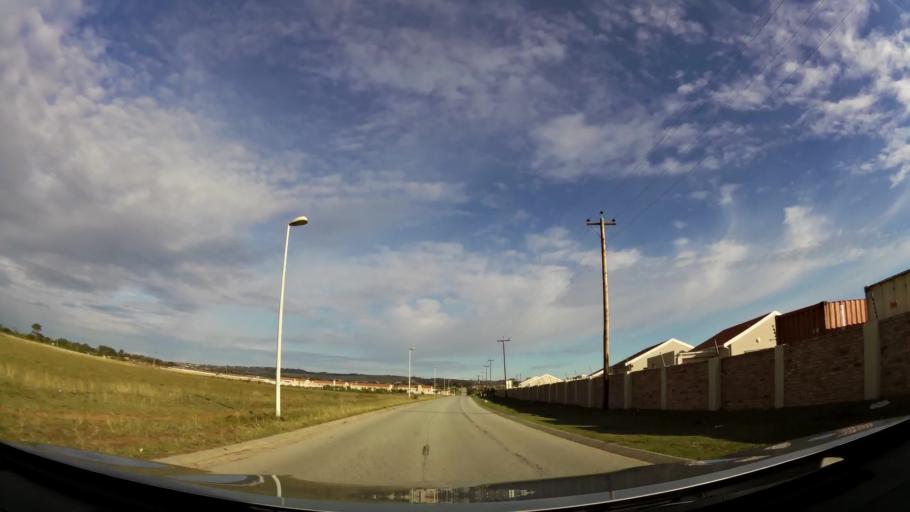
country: ZA
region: Eastern Cape
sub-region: Nelson Mandela Bay Metropolitan Municipality
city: Port Elizabeth
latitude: -33.9502
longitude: 25.4870
